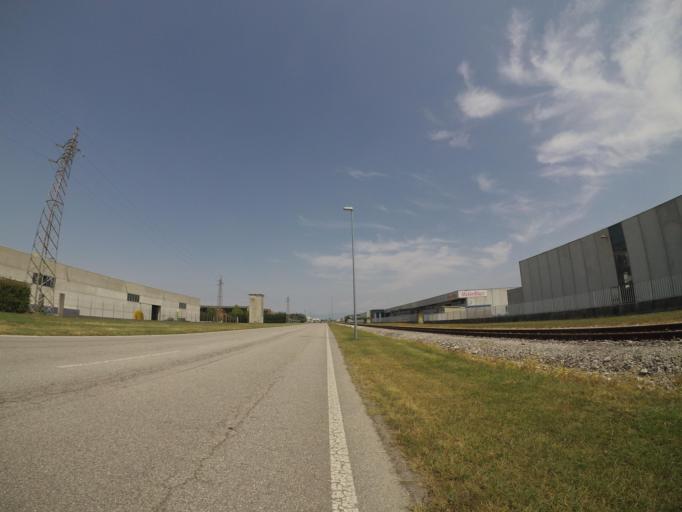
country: IT
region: Friuli Venezia Giulia
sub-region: Provincia di Pordenone
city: Rosa
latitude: 45.9380
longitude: 12.8888
